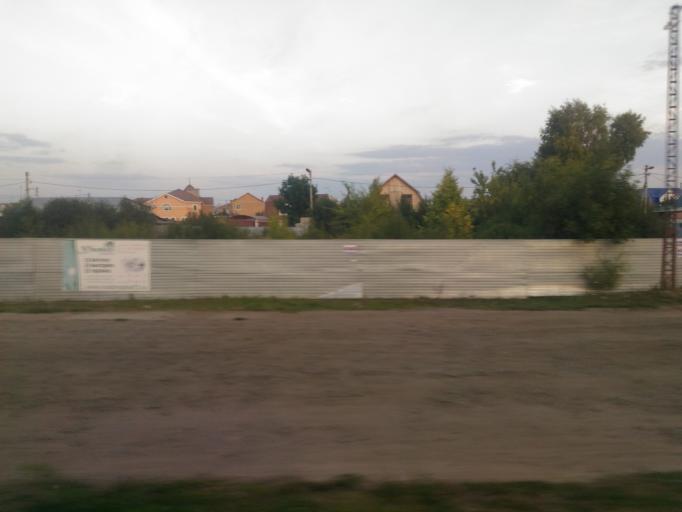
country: RU
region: Ulyanovsk
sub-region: Ulyanovskiy Rayon
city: Ulyanovsk
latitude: 54.2641
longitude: 48.2810
